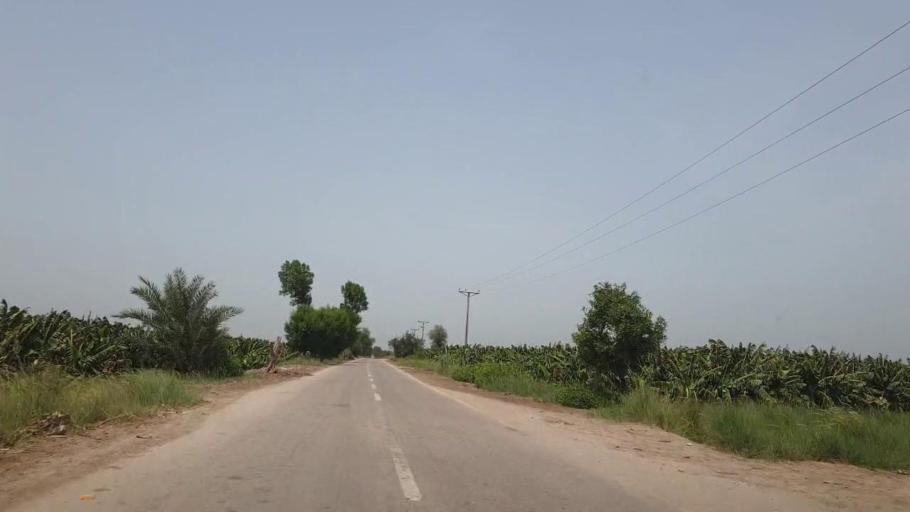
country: PK
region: Sindh
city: Sakrand
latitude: 26.1782
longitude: 68.2276
